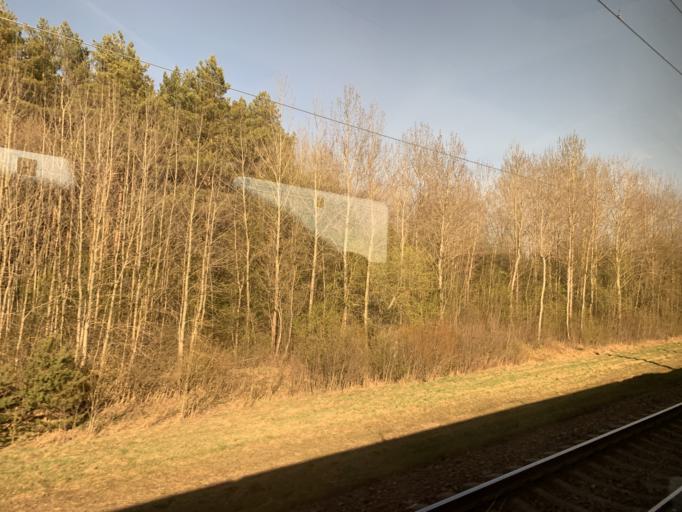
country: BY
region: Grodnenskaya
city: Astravyets
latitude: 54.5756
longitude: 25.9418
